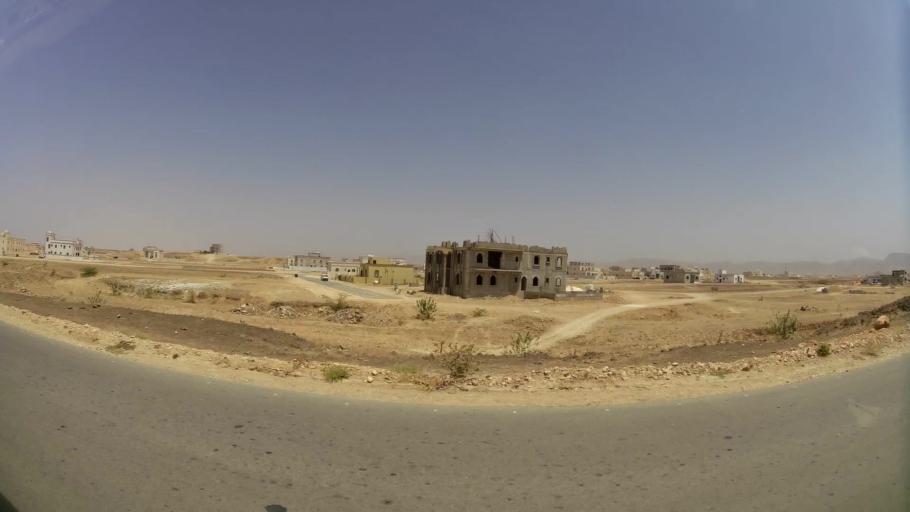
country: OM
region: Zufar
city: Salalah
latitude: 17.0785
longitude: 54.1924
